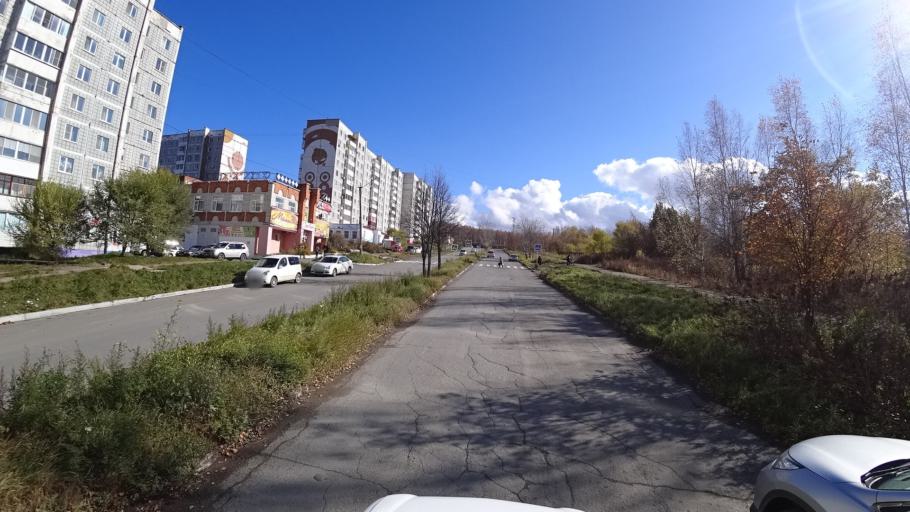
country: RU
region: Khabarovsk Krai
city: Amursk
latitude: 50.2432
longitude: 136.9168
